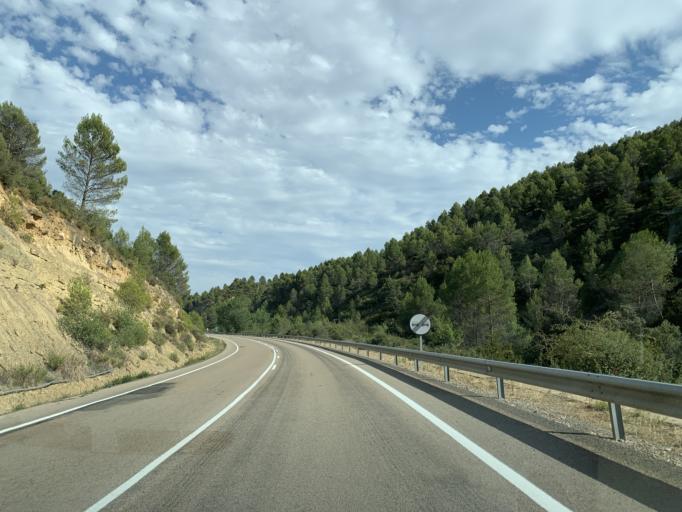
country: ES
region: Aragon
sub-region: Provincia de Zaragoza
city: Santa Eulalia de Gallego
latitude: 42.2962
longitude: -0.7315
